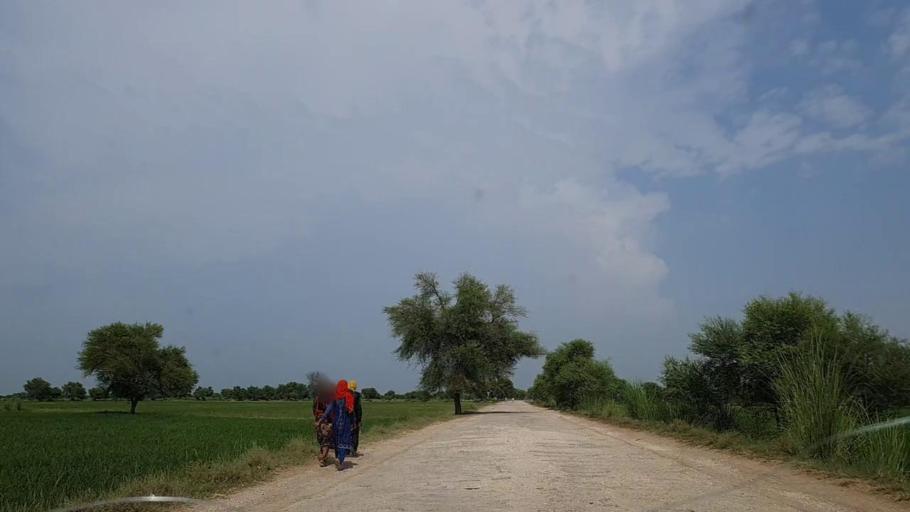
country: PK
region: Sindh
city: Khanpur
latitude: 27.8478
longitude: 69.4291
